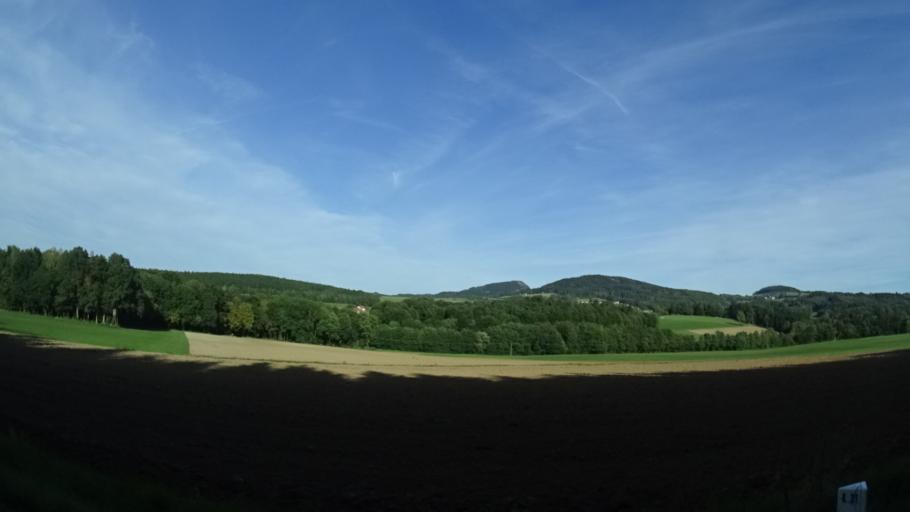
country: DE
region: Hesse
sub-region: Regierungsbezirk Kassel
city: Dipperz
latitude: 50.5385
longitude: 9.8326
